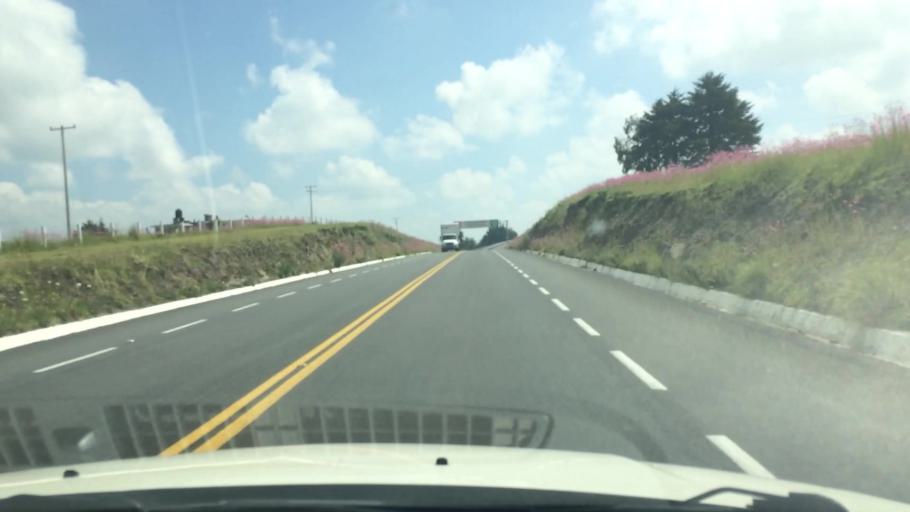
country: MX
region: Mexico
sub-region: Villa Victoria
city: Colonia Doctor Gustavo Baz
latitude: 19.3714
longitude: -99.9326
